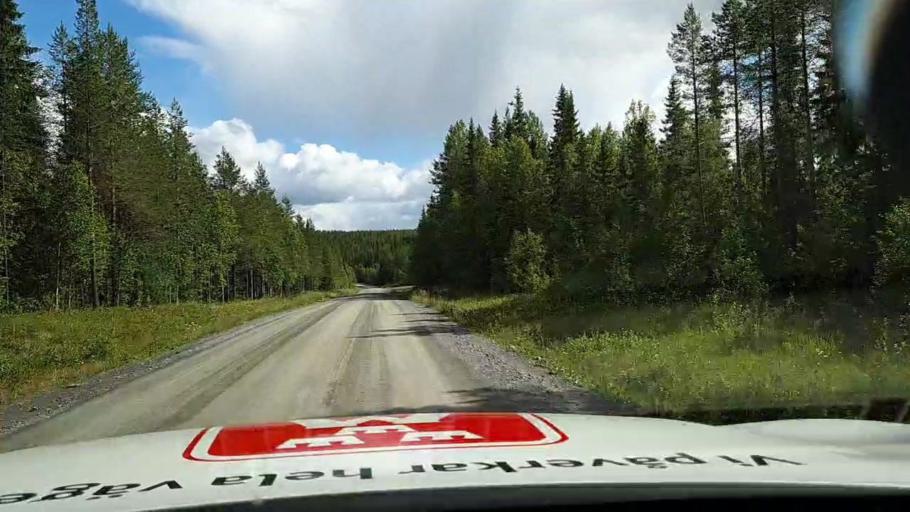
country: SE
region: Jaemtland
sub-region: Krokoms Kommun
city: Valla
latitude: 63.6745
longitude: 13.6955
